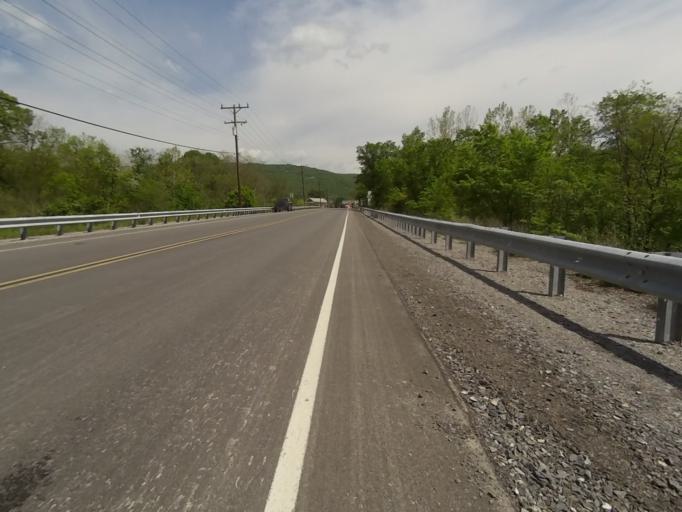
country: US
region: Pennsylvania
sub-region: Centre County
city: Zion
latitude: 41.0162
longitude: -77.6642
